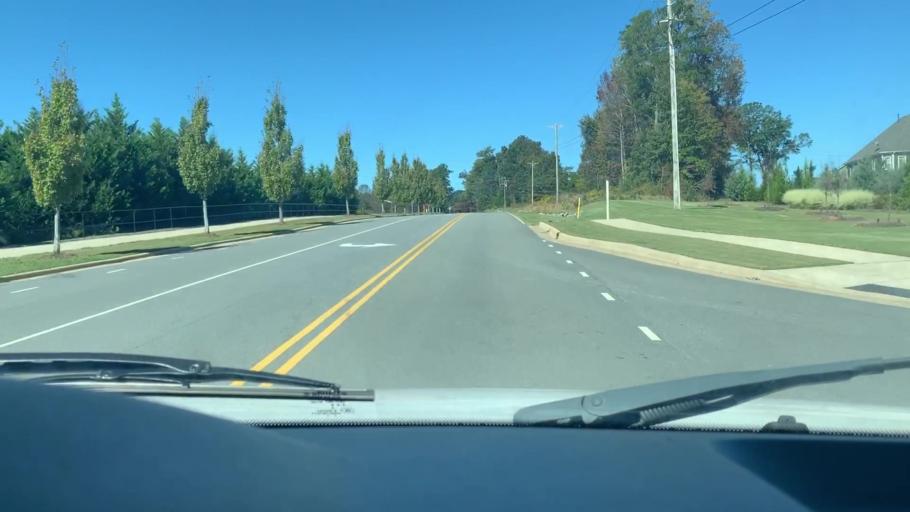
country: US
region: North Carolina
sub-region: Gaston County
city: Davidson
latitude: 35.4685
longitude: -80.8262
